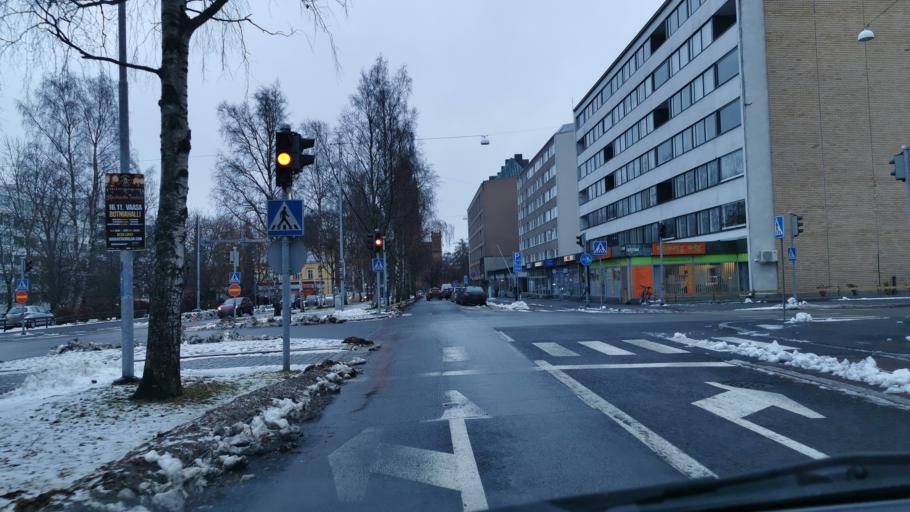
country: FI
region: Ostrobothnia
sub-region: Vaasa
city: Vaasa
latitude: 63.0971
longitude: 21.6078
